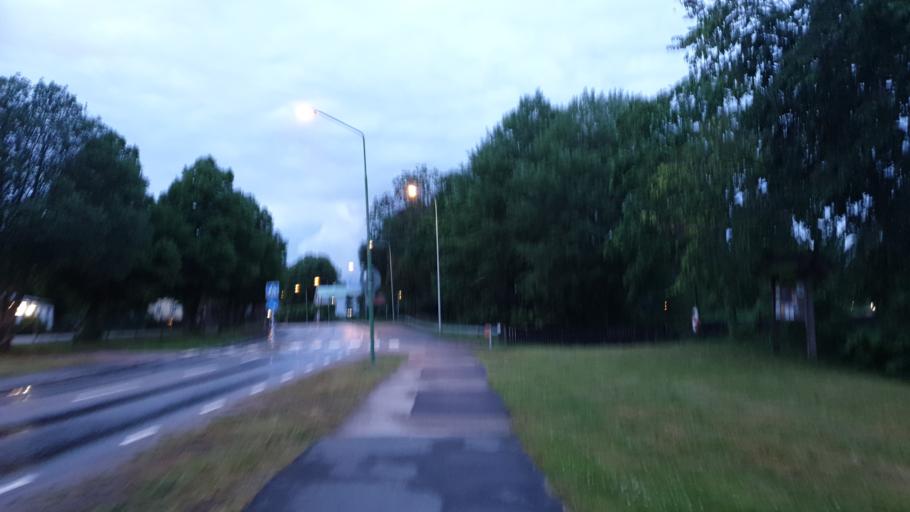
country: SE
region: Kronoberg
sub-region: Ljungby Kommun
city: Ljungby
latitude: 56.8286
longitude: 13.9376
